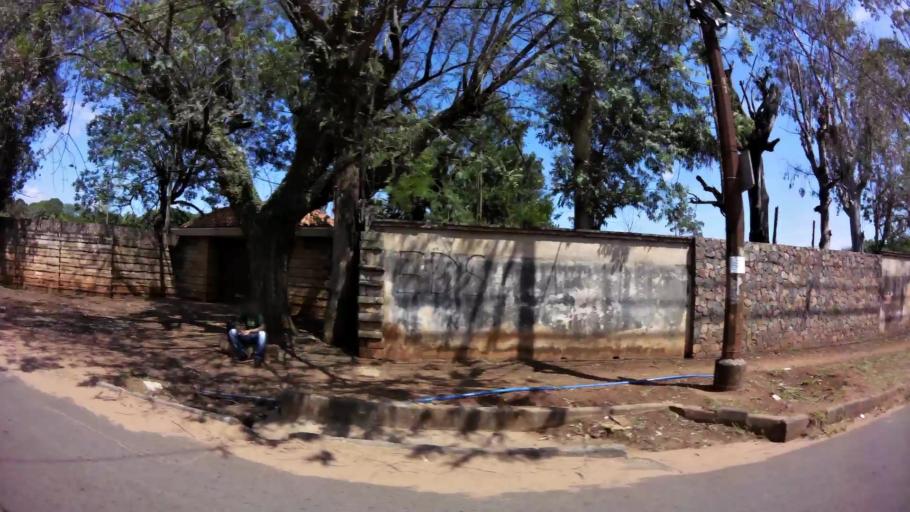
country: PY
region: Central
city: San Lorenzo
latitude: -25.3161
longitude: -57.5074
